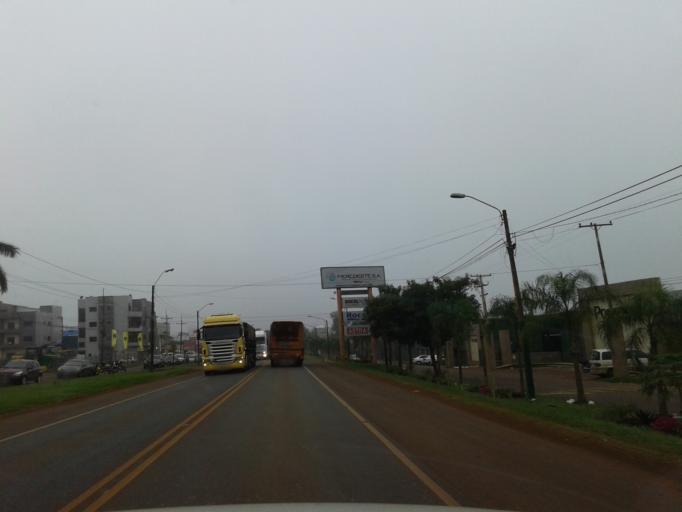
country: PY
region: Alto Parana
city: Santa Rita
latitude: -25.8068
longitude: -55.0987
